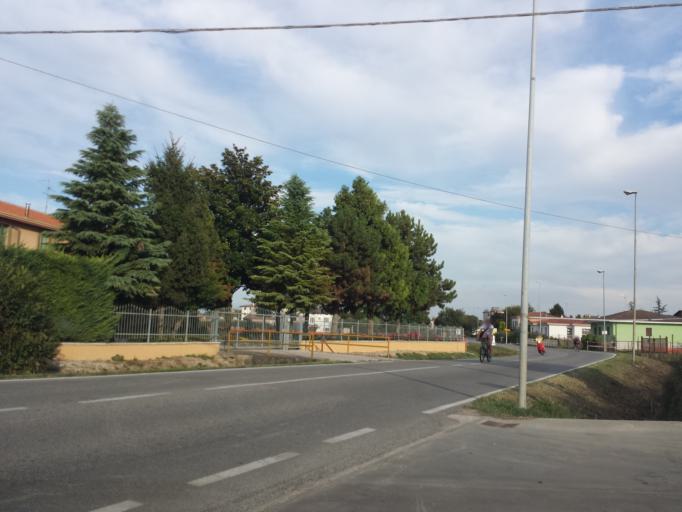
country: IT
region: Veneto
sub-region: Provincia di Verona
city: Isola della Scala
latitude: 45.2756
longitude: 10.9945
